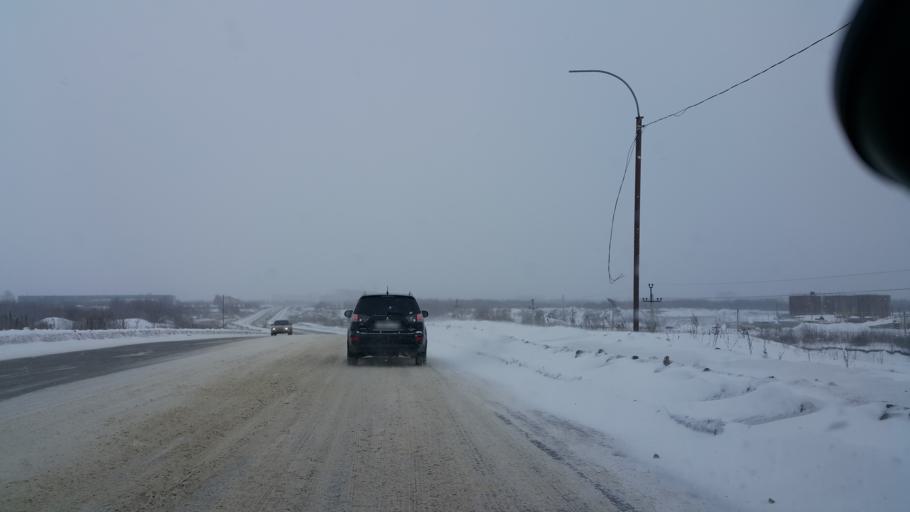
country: RU
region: Tambov
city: Tambov
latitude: 52.7396
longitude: 41.3781
